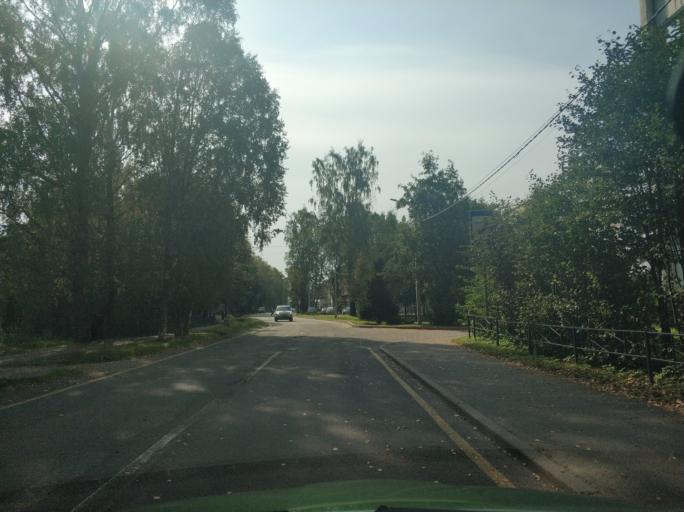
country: RU
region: Leningrad
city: Murino
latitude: 60.0401
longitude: 30.4647
